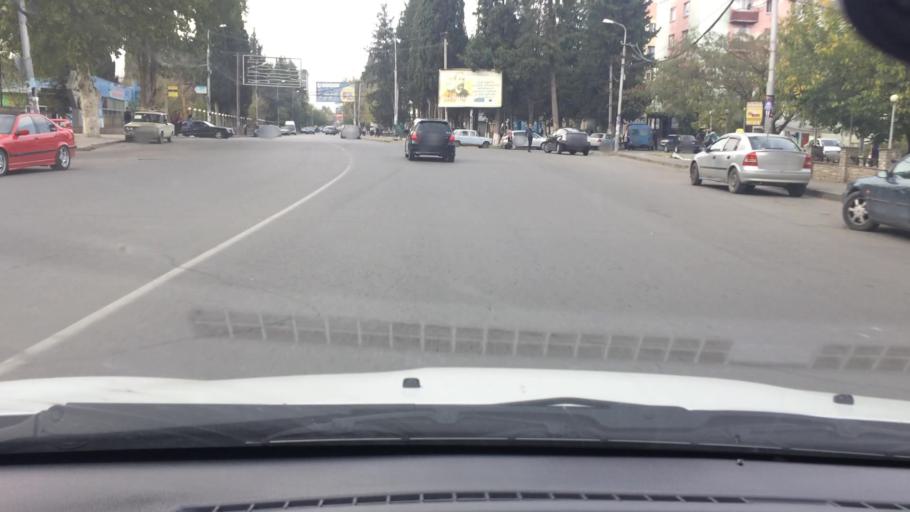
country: GE
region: Kvemo Kartli
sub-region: Marneuli
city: Marneuli
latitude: 41.4731
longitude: 44.8145
